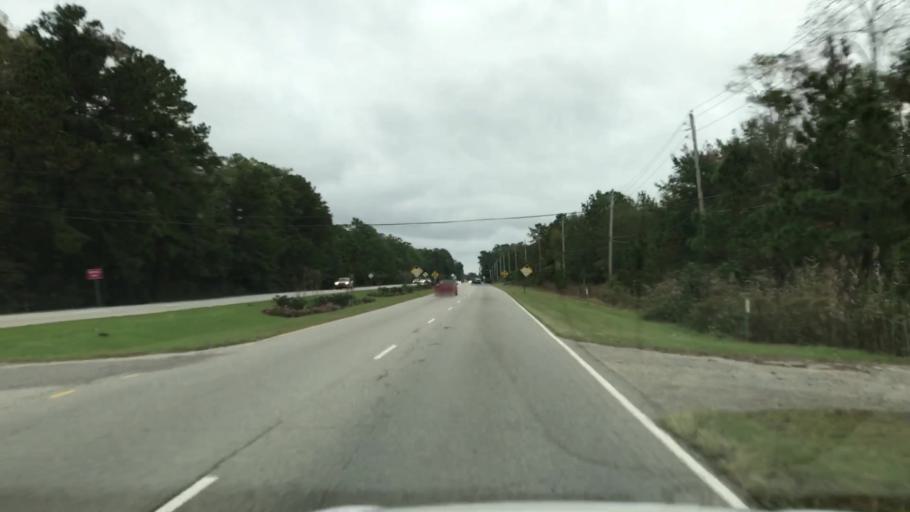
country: US
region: South Carolina
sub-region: Georgetown County
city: Georgetown
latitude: 33.3341
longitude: -79.3086
